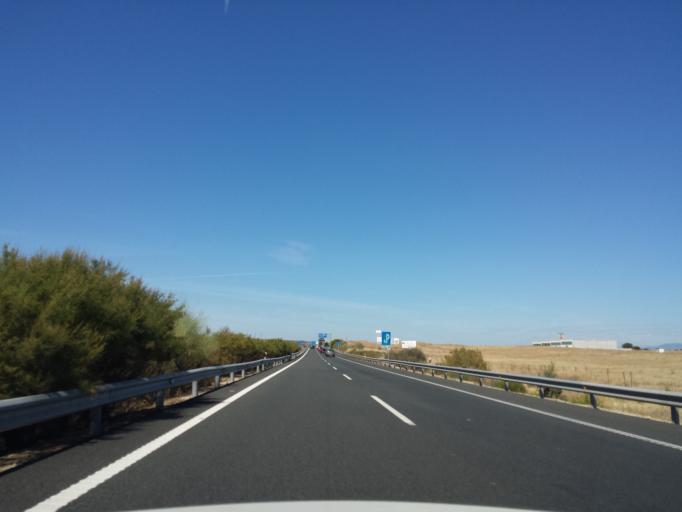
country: ES
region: Extremadura
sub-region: Provincia de Caceres
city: Peraleda de la Mata
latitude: 39.8912
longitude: -5.4150
